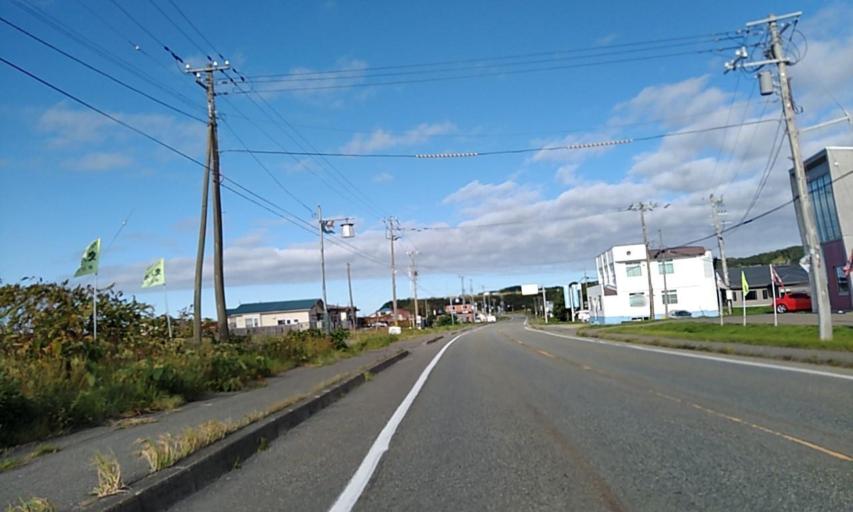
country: JP
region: Hokkaido
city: Shizunai-furukawacho
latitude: 42.2451
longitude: 142.5798
